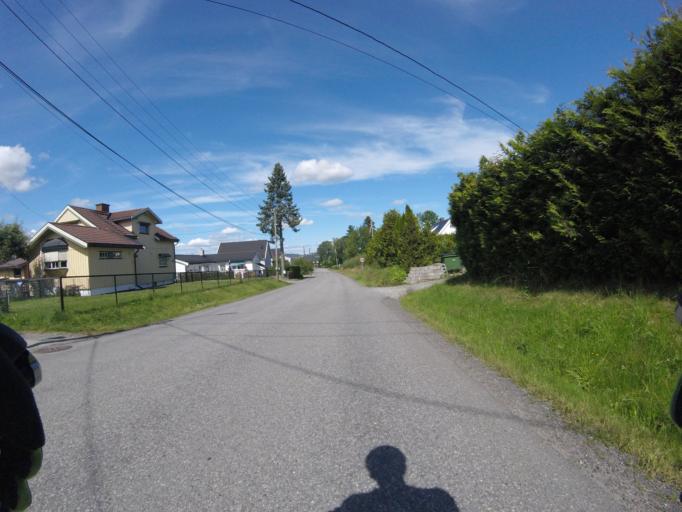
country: NO
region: Akershus
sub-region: Skedsmo
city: Lillestrom
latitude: 59.9486
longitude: 11.0208
